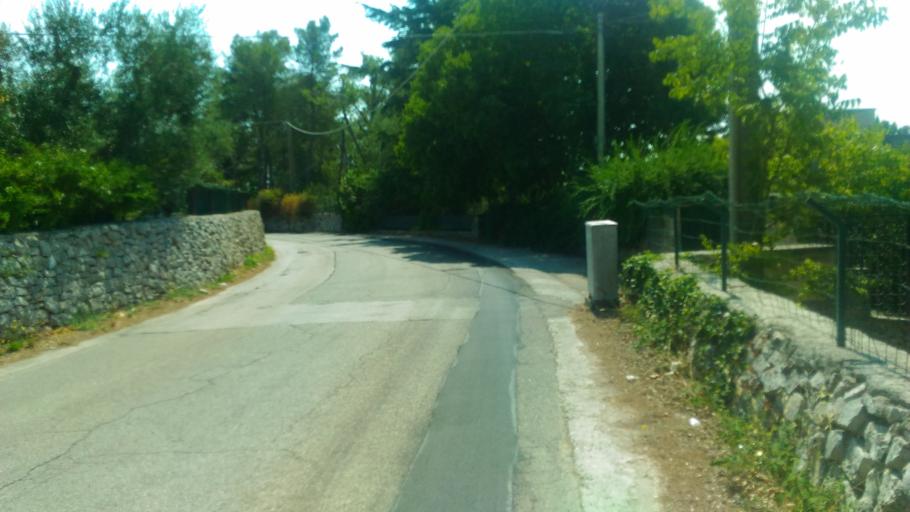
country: IT
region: Apulia
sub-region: Provincia di Bari
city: Locorotondo
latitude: 40.7523
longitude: 17.3398
